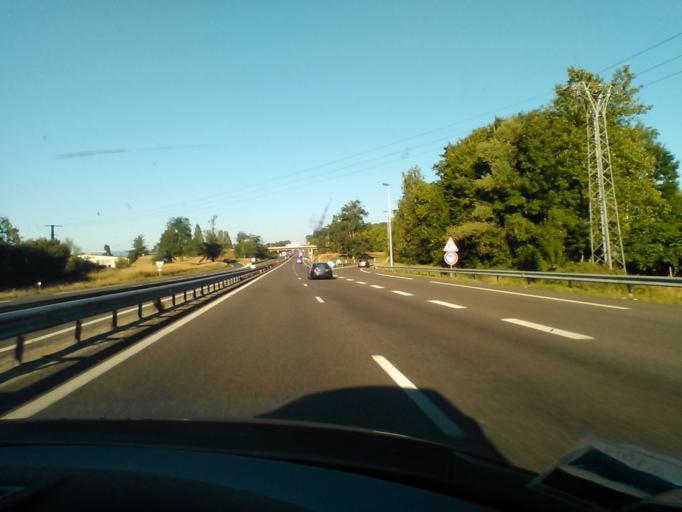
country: FR
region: Rhone-Alpes
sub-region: Departement de l'Isere
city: Saint-Jean-de-Soudain
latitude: 45.5607
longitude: 5.4216
